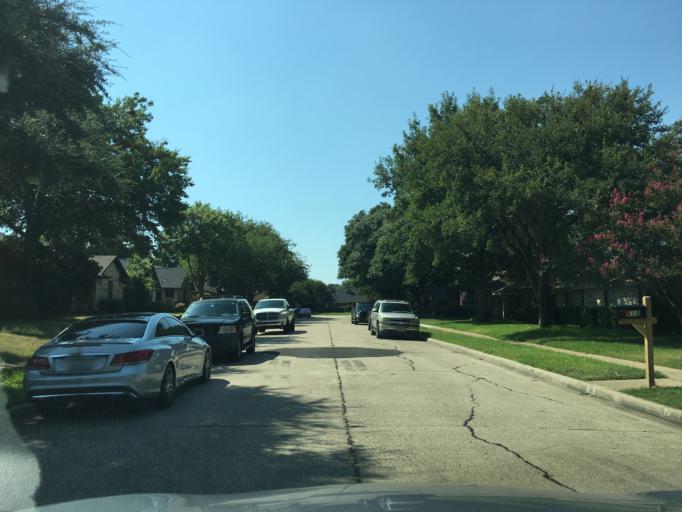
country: US
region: Texas
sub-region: Dallas County
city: Garland
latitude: 32.9362
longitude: -96.6357
